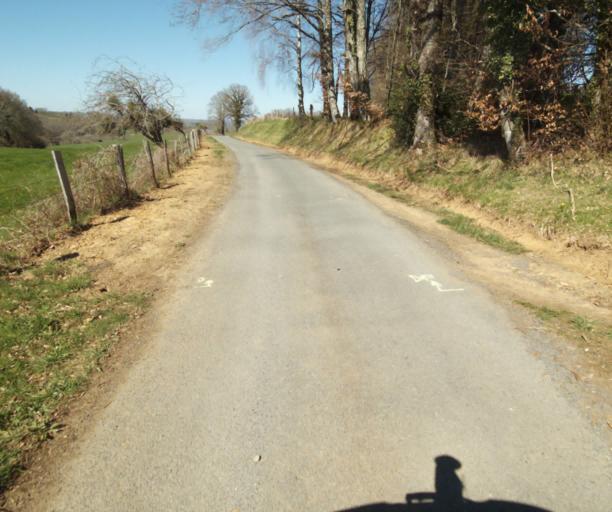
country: FR
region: Limousin
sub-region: Departement de la Correze
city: Uzerche
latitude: 45.3964
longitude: 1.6091
